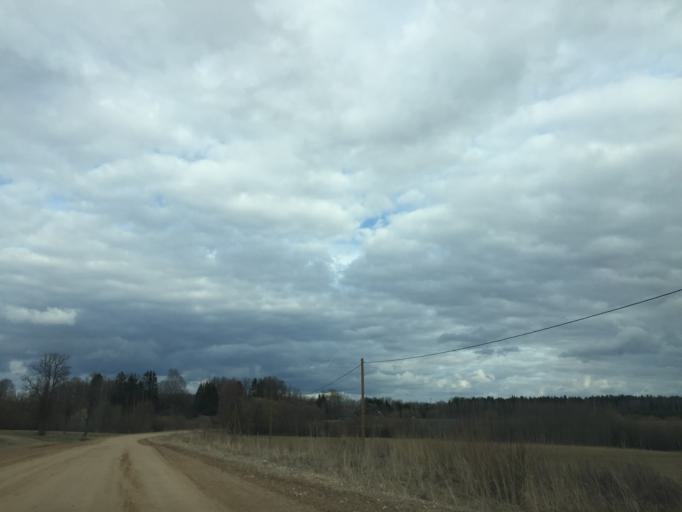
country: LV
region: Lielvarde
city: Lielvarde
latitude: 56.5248
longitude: 24.7658
